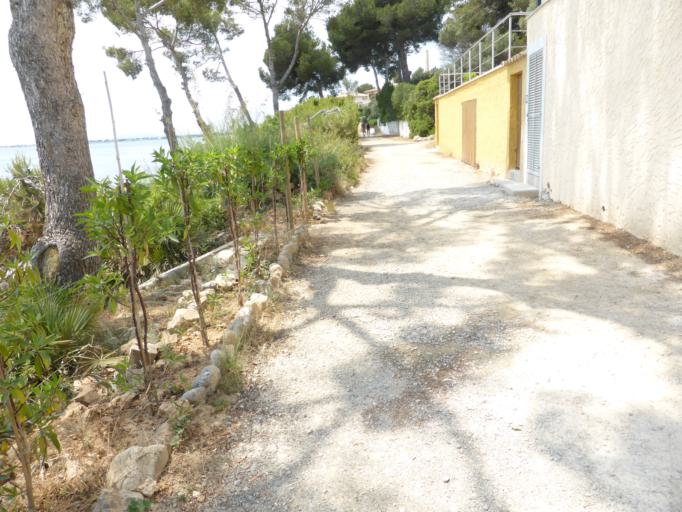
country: ES
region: Balearic Islands
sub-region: Illes Balears
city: Port d'Alcudia
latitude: 39.8360
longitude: 3.1529
